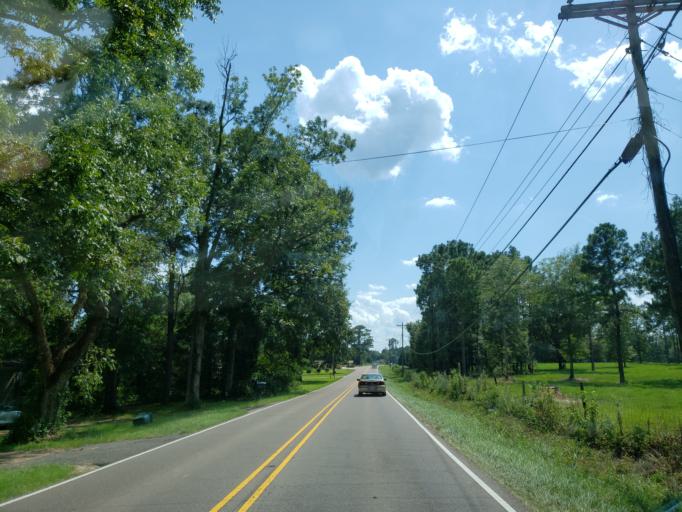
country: US
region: Mississippi
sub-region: Lamar County
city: West Hattiesburg
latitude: 31.2930
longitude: -89.3907
